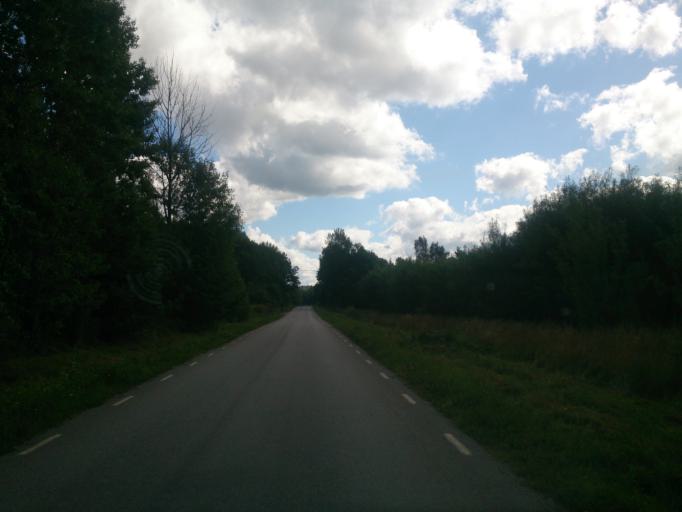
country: SE
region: OEstergoetland
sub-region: Atvidabergs Kommun
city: Atvidaberg
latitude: 58.3354
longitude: 16.0092
